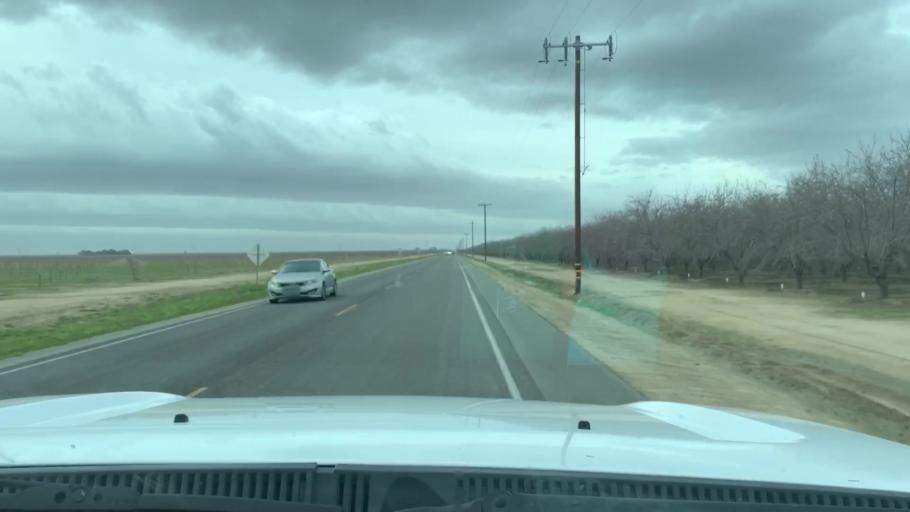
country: US
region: California
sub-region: Kern County
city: Wasco
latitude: 35.5582
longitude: -119.2970
